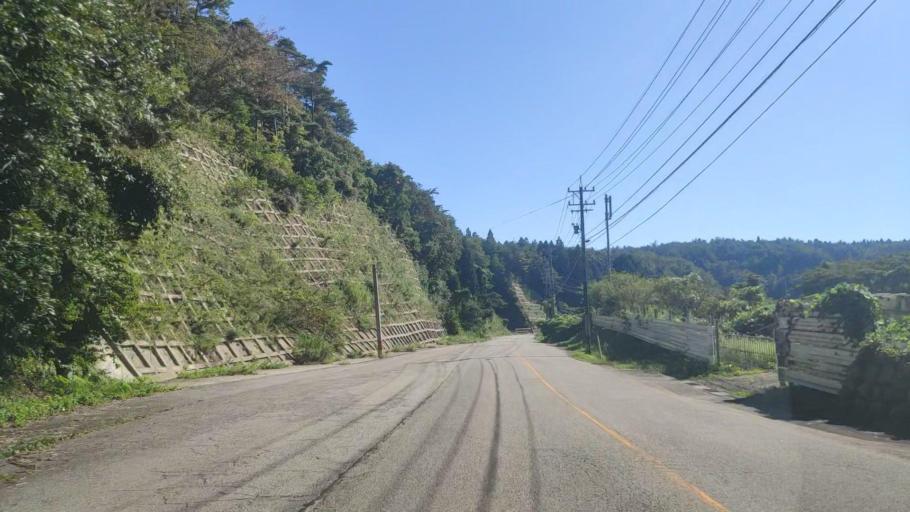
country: JP
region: Ishikawa
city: Nanao
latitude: 37.3179
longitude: 137.1650
